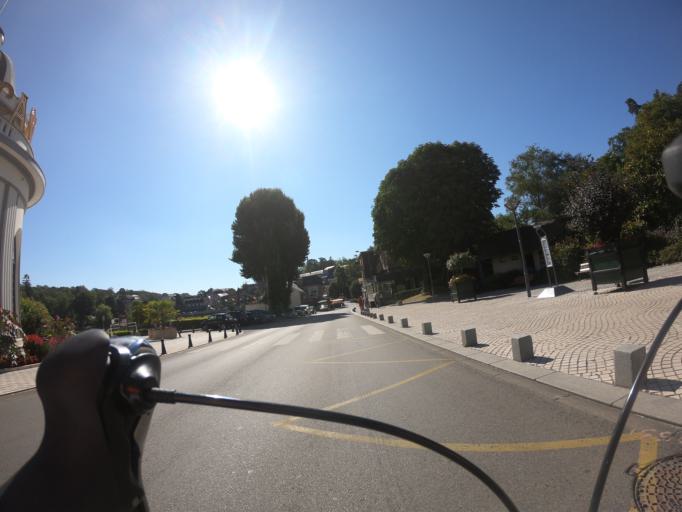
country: FR
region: Lower Normandy
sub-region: Departement de l'Orne
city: Tesse-la-Madeleine
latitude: 48.5576
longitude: -0.4185
